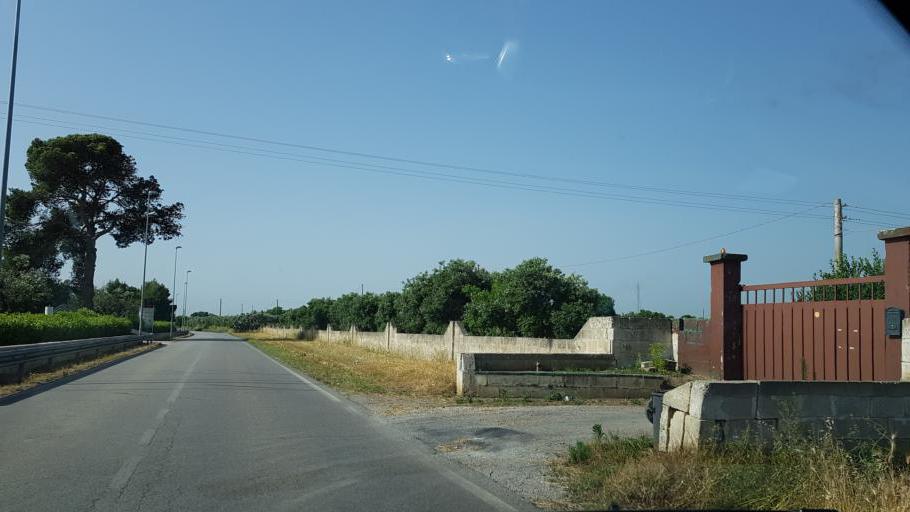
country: IT
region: Apulia
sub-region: Provincia di Brindisi
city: Mesagne
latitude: 40.5413
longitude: 17.8167
